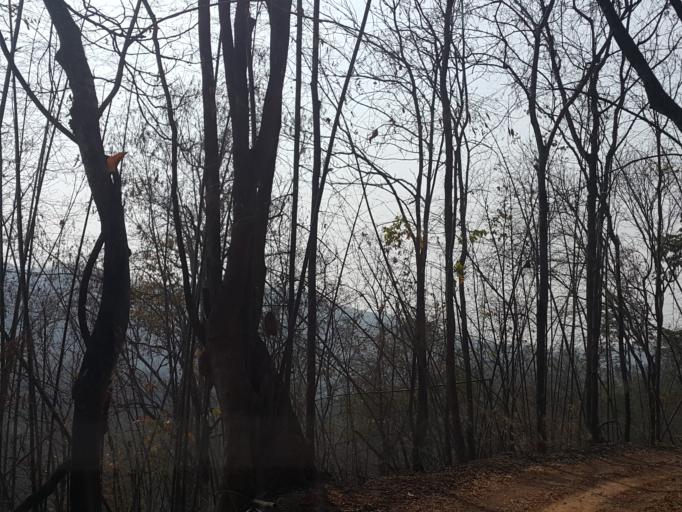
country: TH
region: Chiang Mai
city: Hang Dong
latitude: 18.7507
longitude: 98.8576
